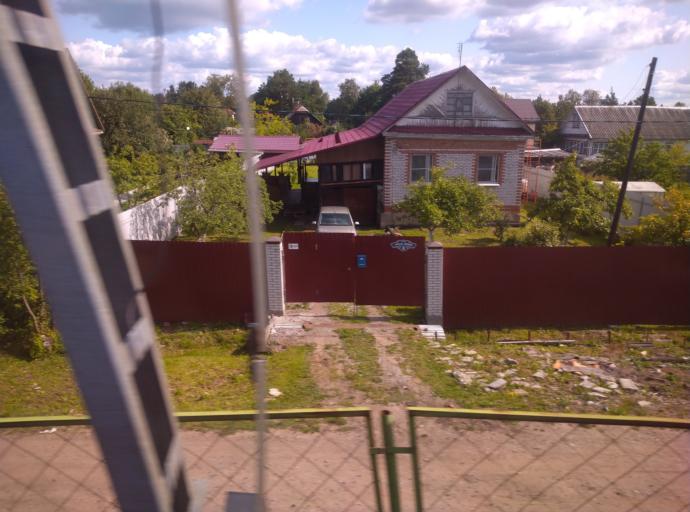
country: RU
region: Leningrad
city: Ul'yanovka
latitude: 59.6408
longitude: 30.7506
